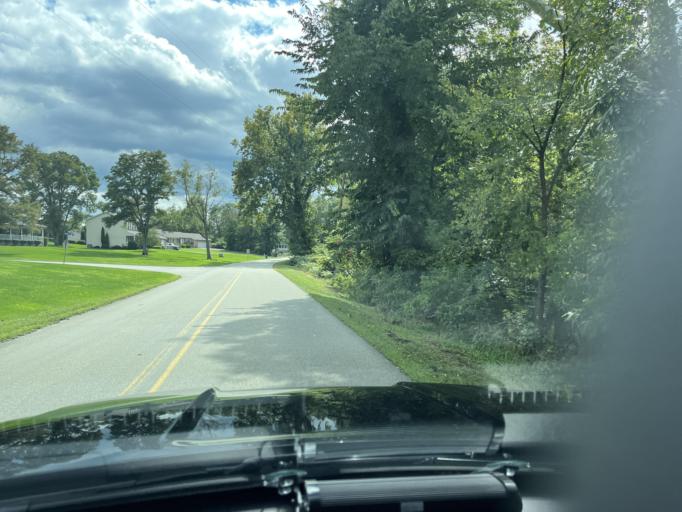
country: US
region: Pennsylvania
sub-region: Fayette County
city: Hopwood
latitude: 39.8843
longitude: -79.7154
